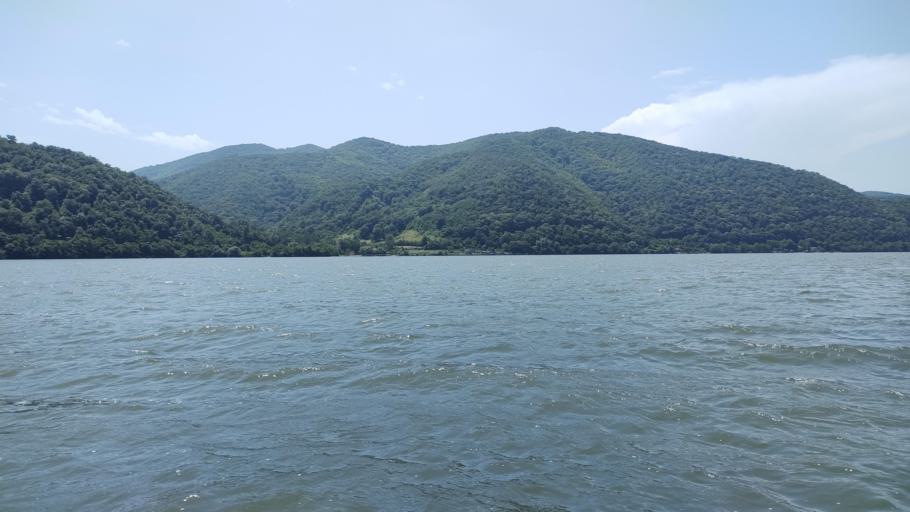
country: RO
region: Caras-Severin
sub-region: Comuna Berzasca
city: Berzasca
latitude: 44.6361
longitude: 21.9652
